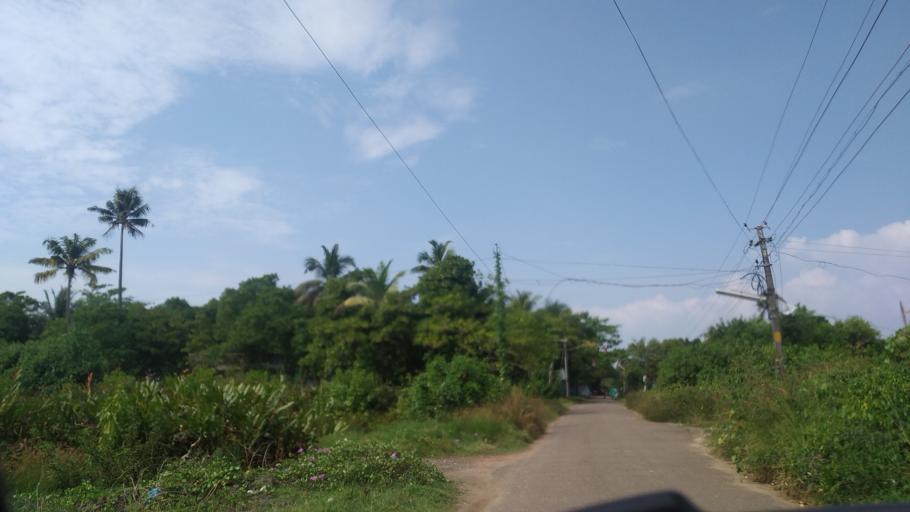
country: IN
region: Kerala
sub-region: Ernakulam
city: Elur
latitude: 10.0542
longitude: 76.2025
